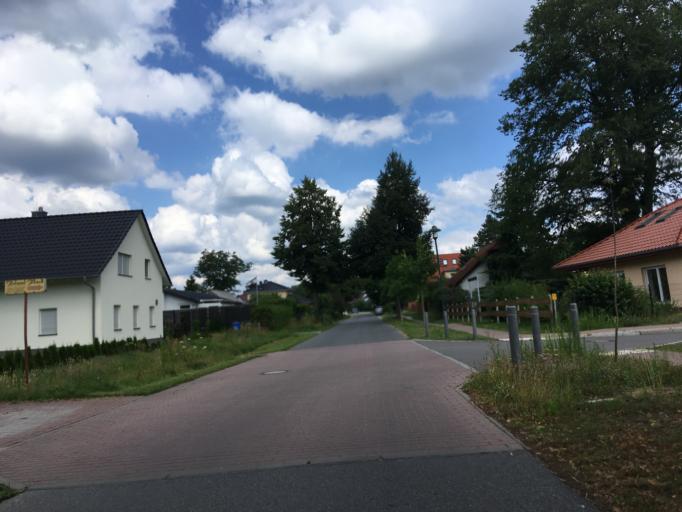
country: DE
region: Berlin
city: Buch
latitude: 52.6728
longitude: 13.5249
